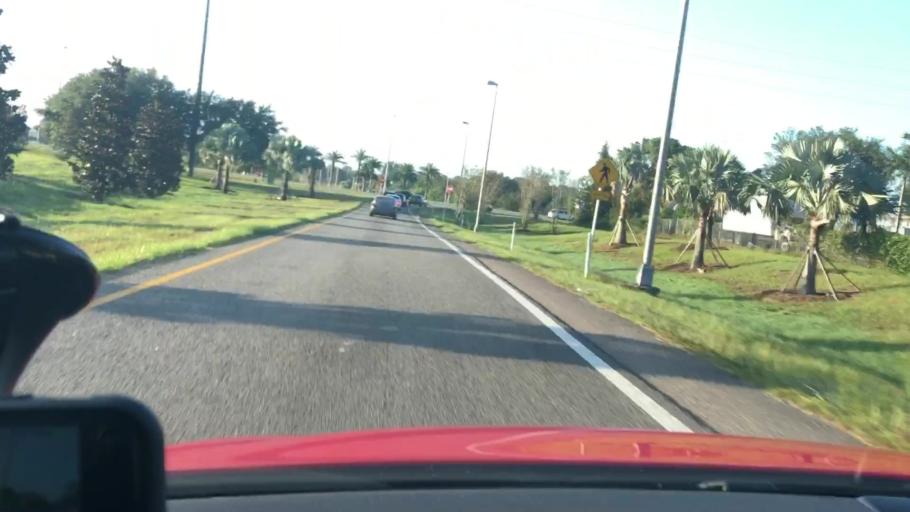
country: US
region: Florida
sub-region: Volusia County
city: Deltona
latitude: 28.9124
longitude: -81.2742
